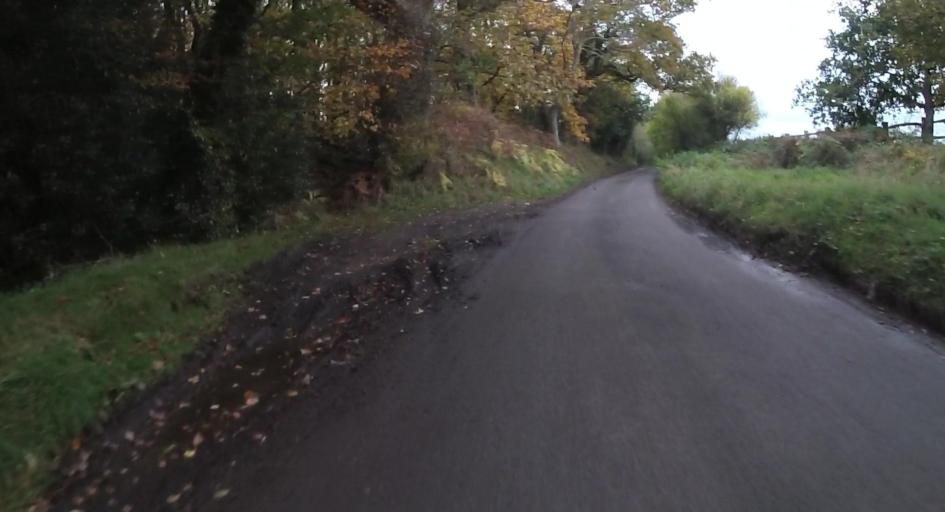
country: GB
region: England
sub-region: Surrey
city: Churt
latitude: 51.1428
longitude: -0.7977
